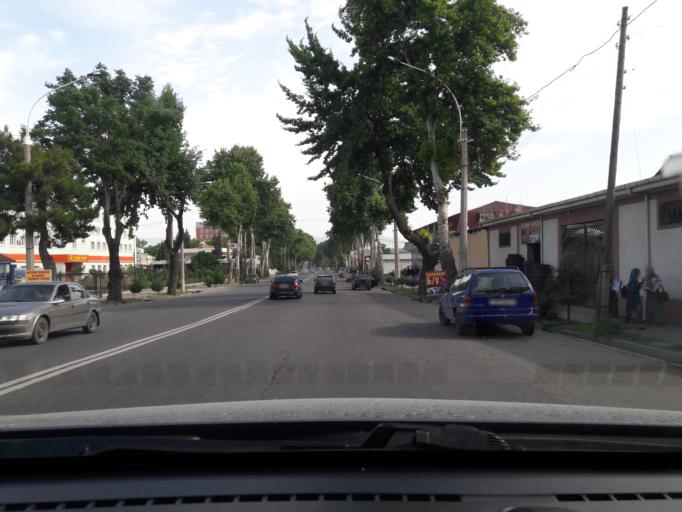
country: TJ
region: Dushanbe
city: Dushanbe
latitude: 38.5362
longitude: 68.7717
